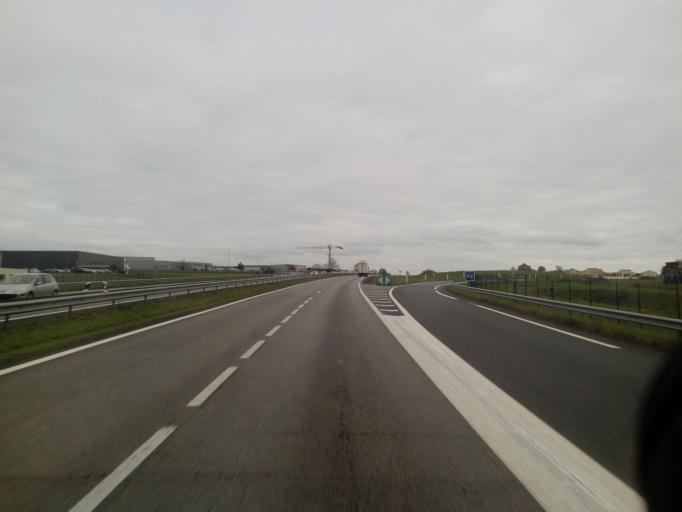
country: FR
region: Pays de la Loire
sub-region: Departement de Maine-et-Loire
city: La Seguiniere
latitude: 47.0753
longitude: -0.9455
